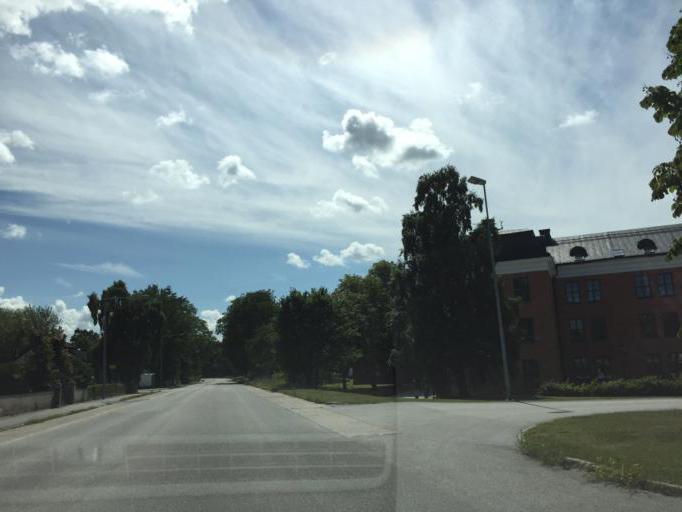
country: SE
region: Gotland
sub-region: Gotland
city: Visby
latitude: 57.6143
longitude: 18.2848
